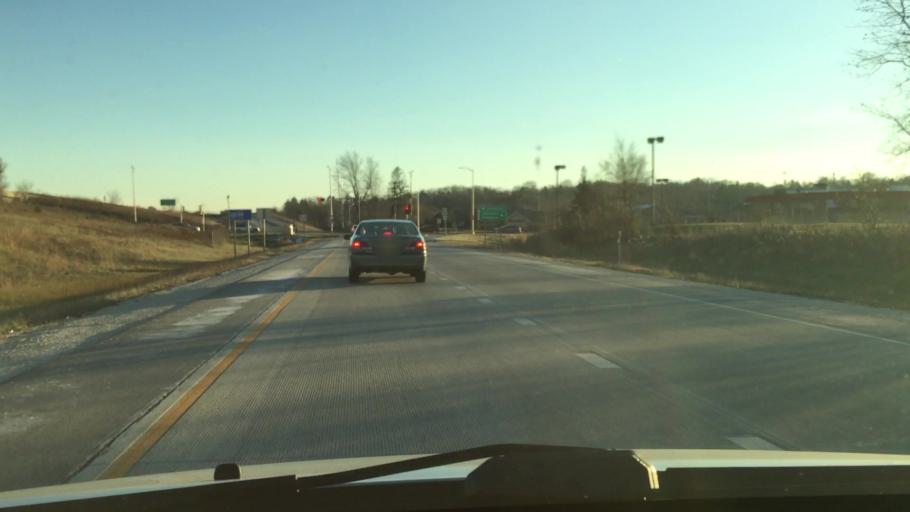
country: US
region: Wisconsin
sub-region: Waukesha County
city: Pewaukee
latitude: 43.0847
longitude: -88.2521
